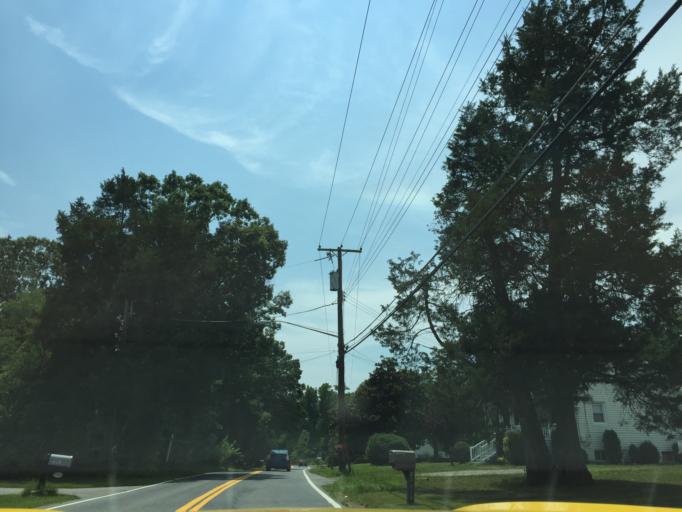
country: US
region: Maryland
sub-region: Prince George's County
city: Friendly
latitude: 38.7177
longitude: -76.9848
